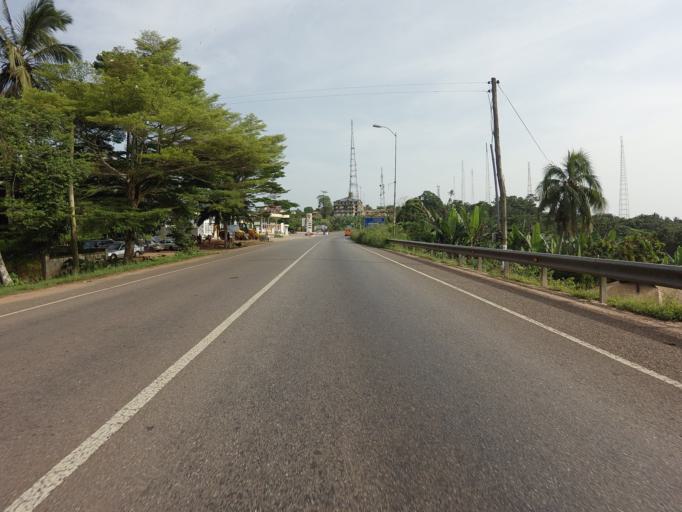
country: GH
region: Eastern
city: Aburi
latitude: 5.8554
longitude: -0.1690
